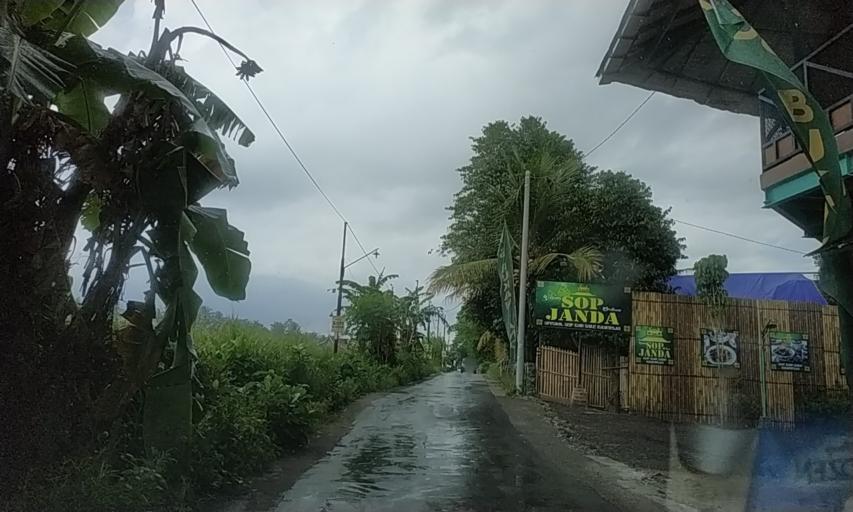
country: ID
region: Daerah Istimewa Yogyakarta
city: Sleman
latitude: -7.6706
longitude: 110.4195
